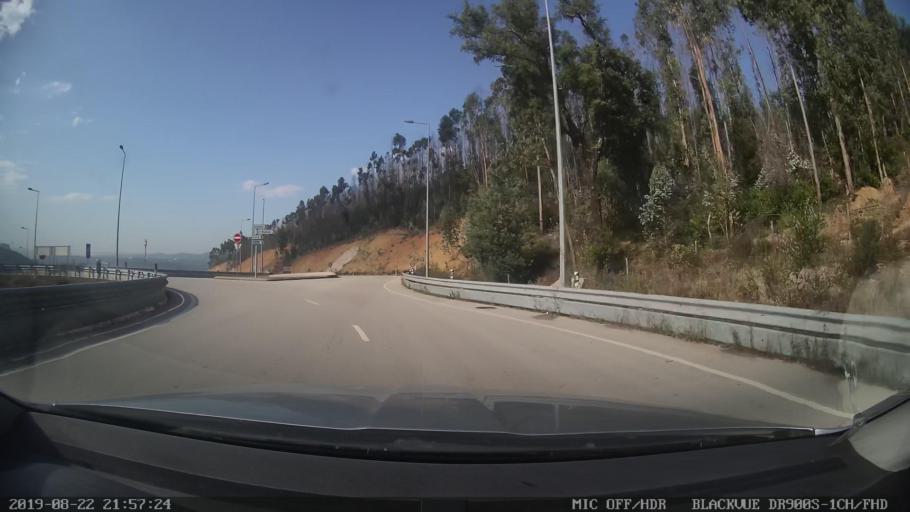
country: PT
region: Coimbra
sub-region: Coimbra
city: Coimbra
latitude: 40.1834
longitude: -8.3796
